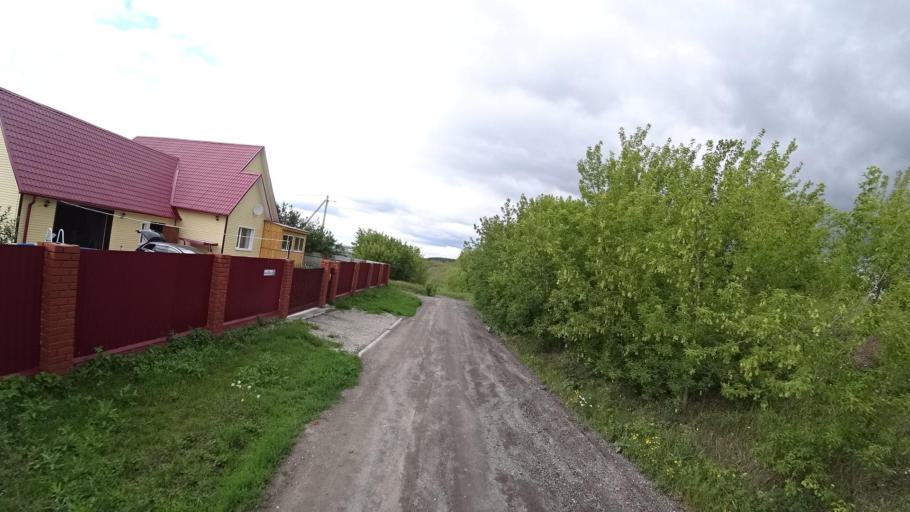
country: RU
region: Sverdlovsk
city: Kamyshlov
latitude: 56.8550
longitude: 62.7187
